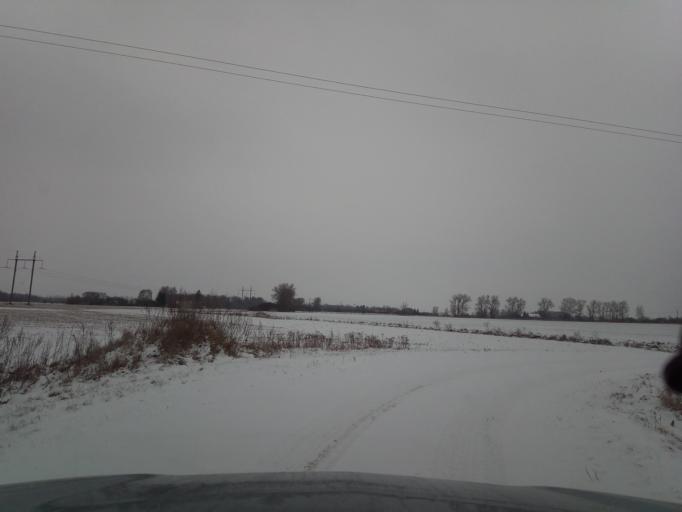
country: LT
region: Panevezys
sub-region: Panevezys City
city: Panevezys
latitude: 55.6275
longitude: 24.3383
